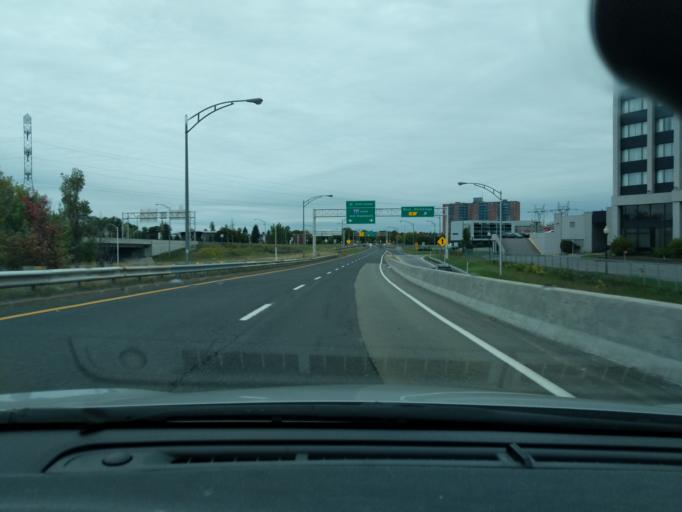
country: CA
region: Quebec
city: L'Ancienne-Lorette
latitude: 46.7622
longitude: -71.2998
